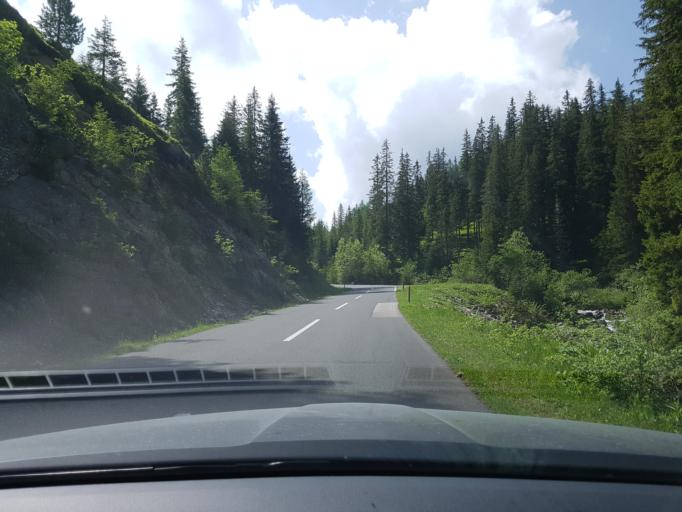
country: AT
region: Salzburg
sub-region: Politischer Bezirk Tamsweg
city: Thomatal
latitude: 46.9630
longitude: 13.7280
